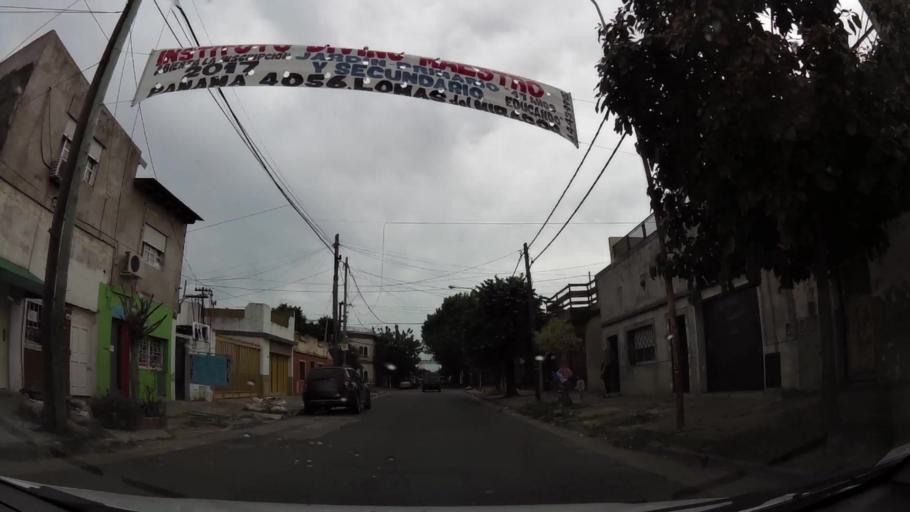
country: AR
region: Buenos Aires
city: San Justo
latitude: -34.6703
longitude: -58.5225
